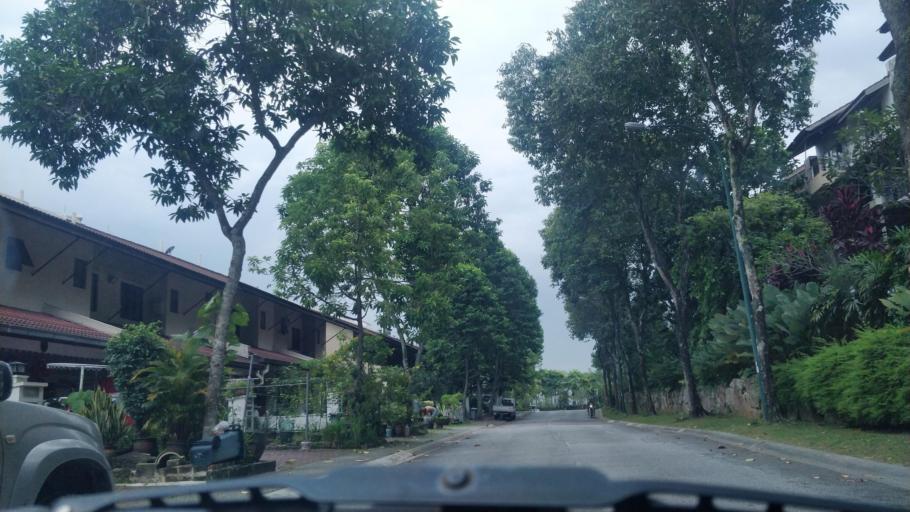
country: MY
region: Selangor
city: Kuang
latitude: 3.2095
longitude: 101.5808
